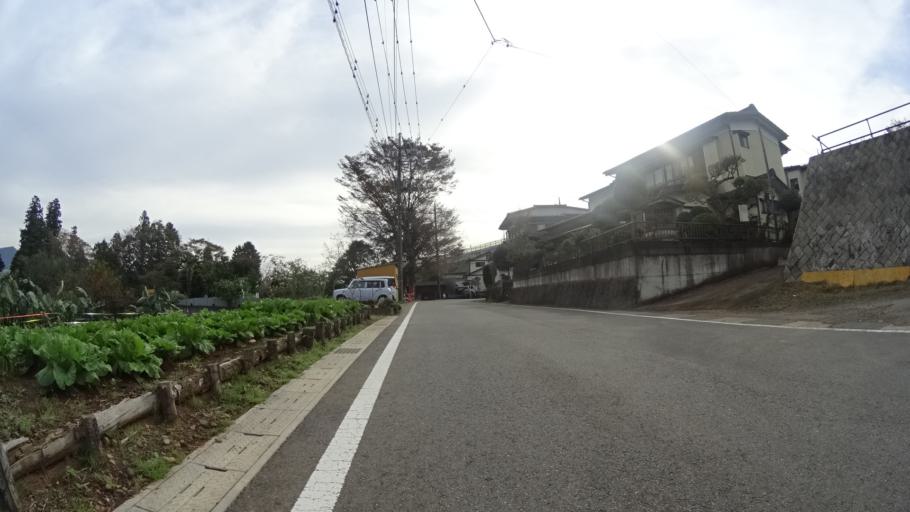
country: JP
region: Yamanashi
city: Uenohara
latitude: 35.6343
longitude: 139.0610
